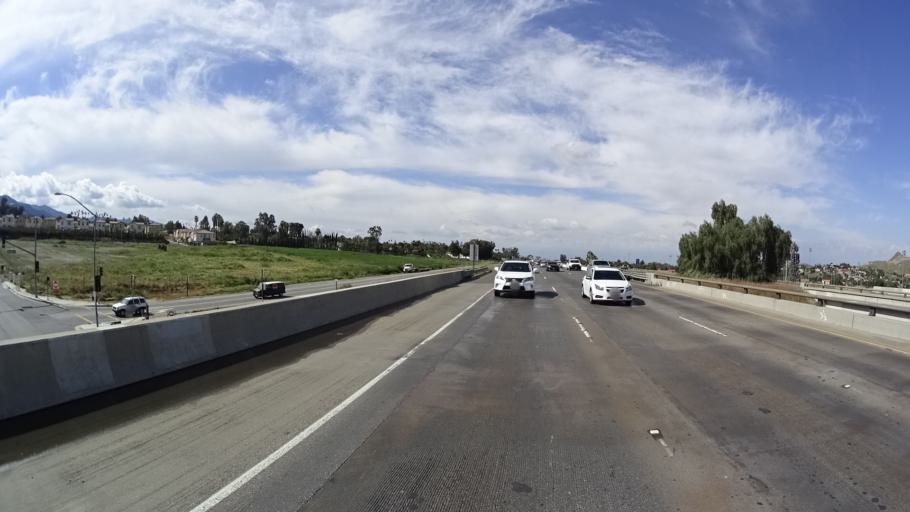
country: US
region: California
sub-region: Riverside County
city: El Cerrito
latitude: 33.8320
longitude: -117.5300
